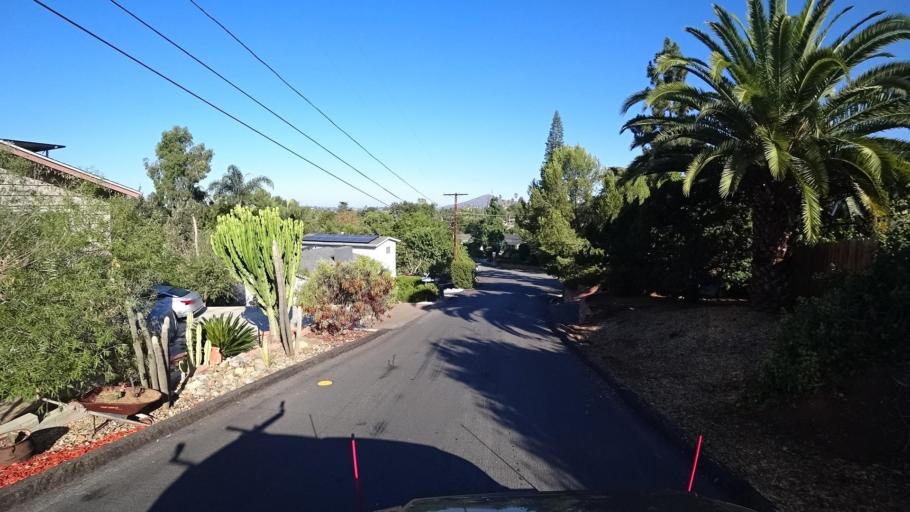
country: US
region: California
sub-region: San Diego County
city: Spring Valley
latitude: 32.7644
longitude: -116.9956
